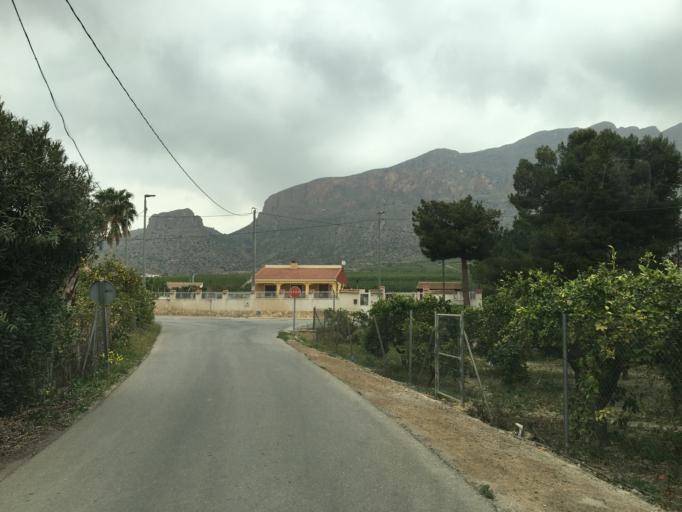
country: ES
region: Murcia
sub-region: Murcia
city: Santomera
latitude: 38.0747
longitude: -1.0305
